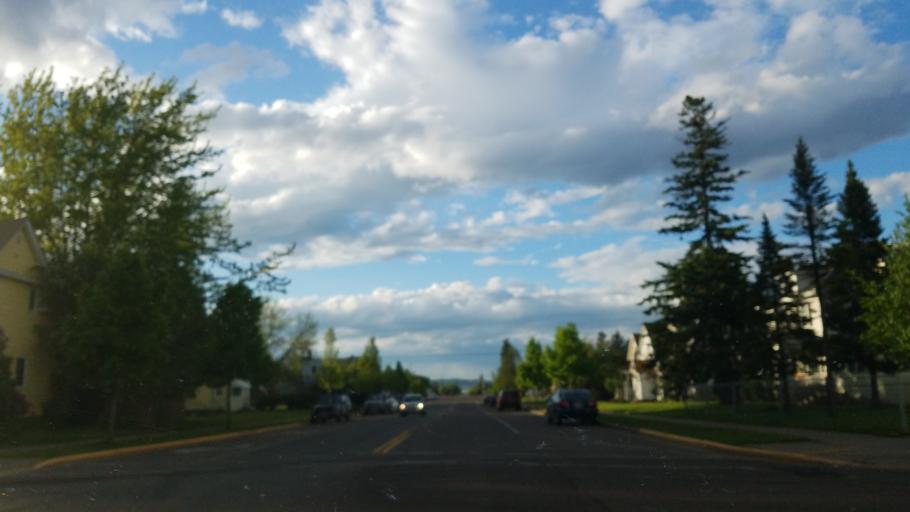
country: US
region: Wisconsin
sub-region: Douglas County
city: Superior
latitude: 46.7251
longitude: -92.0934
